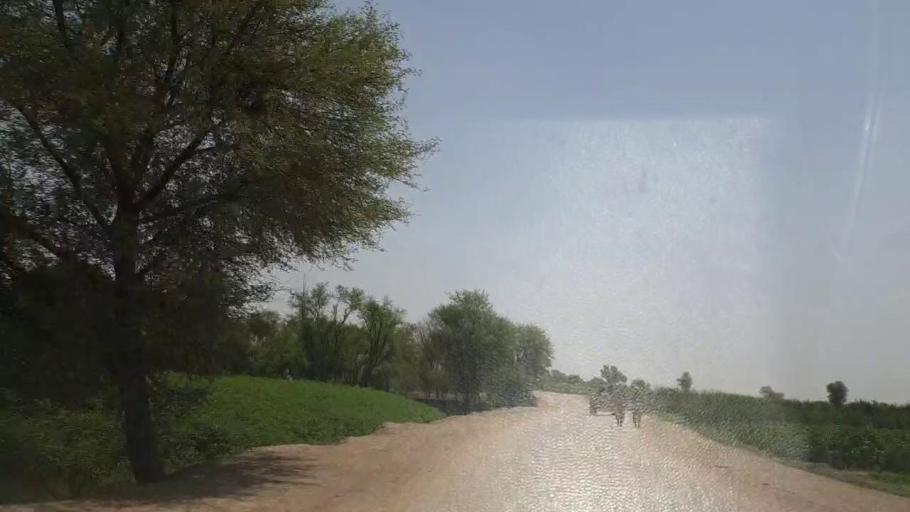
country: PK
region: Sindh
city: Bozdar
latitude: 27.2490
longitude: 68.6761
